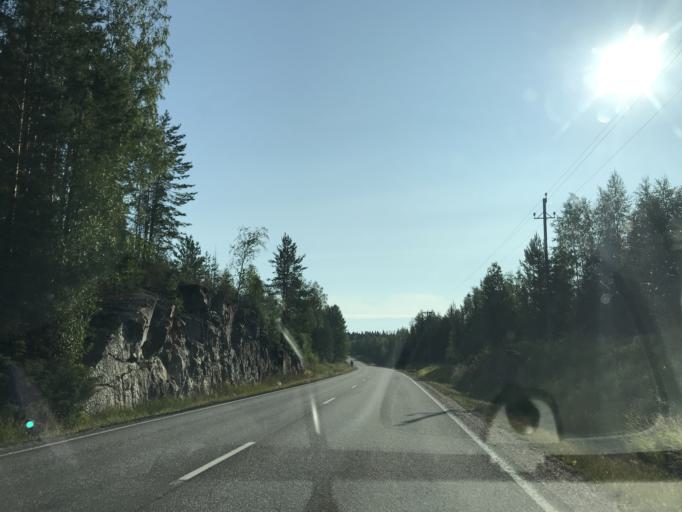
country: FI
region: Paijanne Tavastia
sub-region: Lahti
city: Orimattila
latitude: 60.7865
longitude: 25.6265
